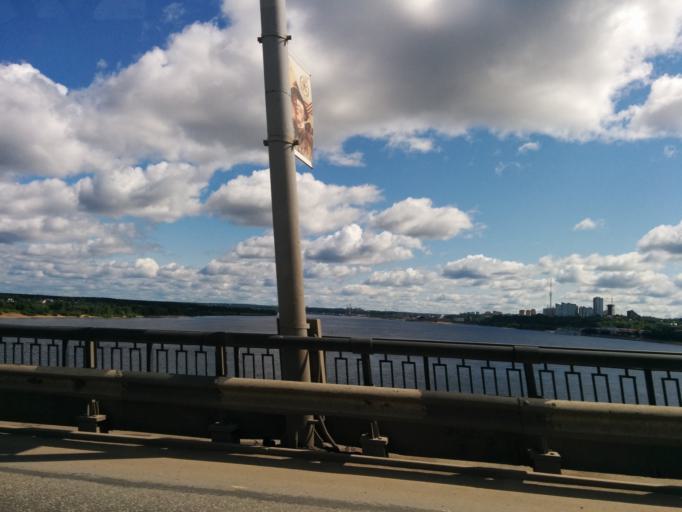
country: RU
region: Perm
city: Perm
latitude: 58.0198
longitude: 56.2213
